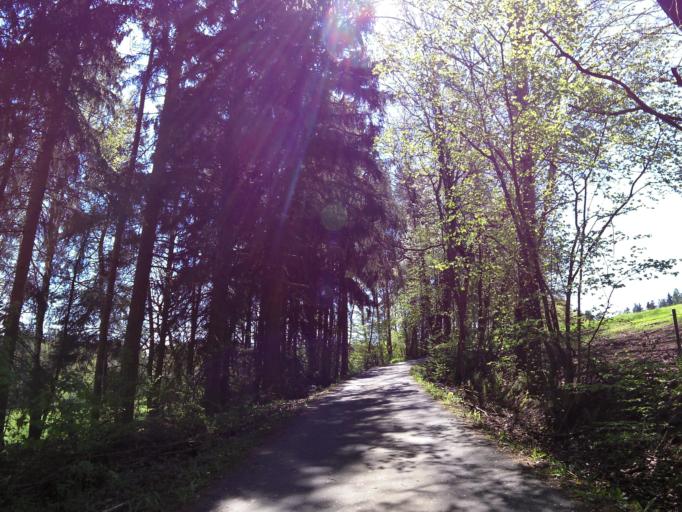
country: DE
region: Thuringia
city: Bad Salzungen
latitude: 50.8327
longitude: 10.2555
